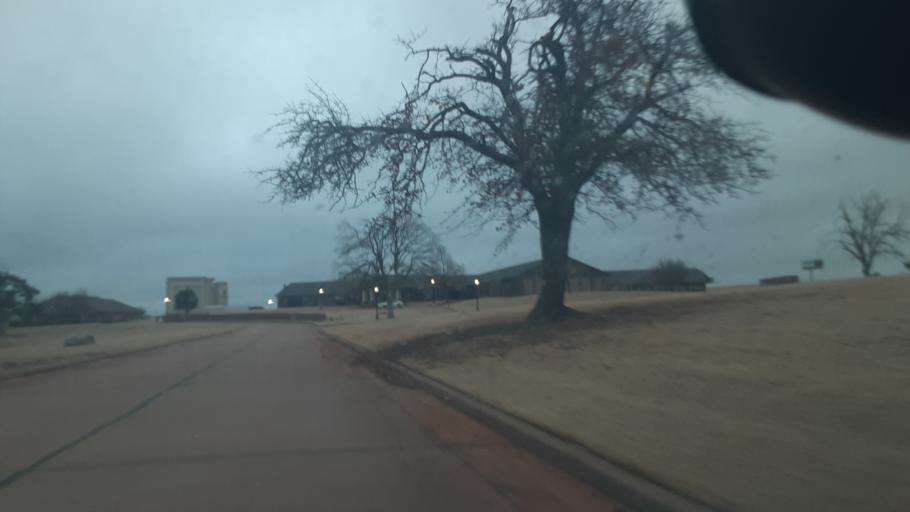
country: US
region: Oklahoma
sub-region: Logan County
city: Guthrie
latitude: 35.8744
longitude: -97.3994
